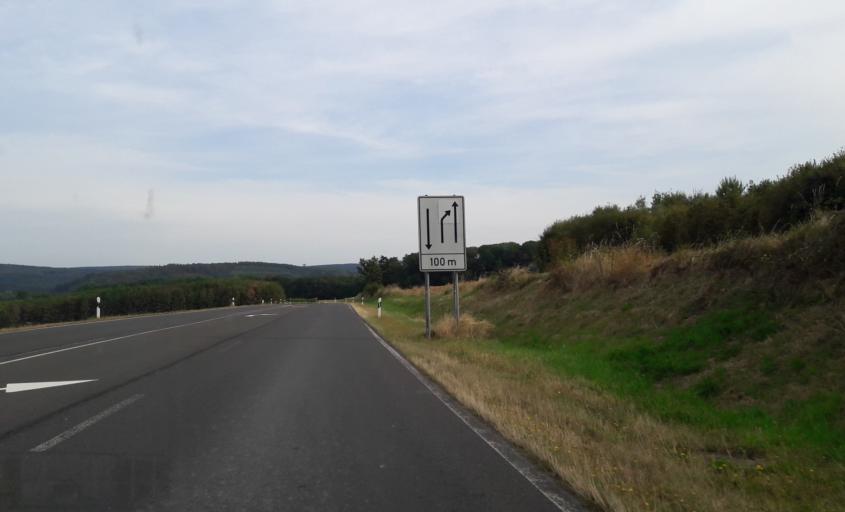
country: DE
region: Rheinland-Pfalz
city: Rinzenberg
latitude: 49.6690
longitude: 7.1455
